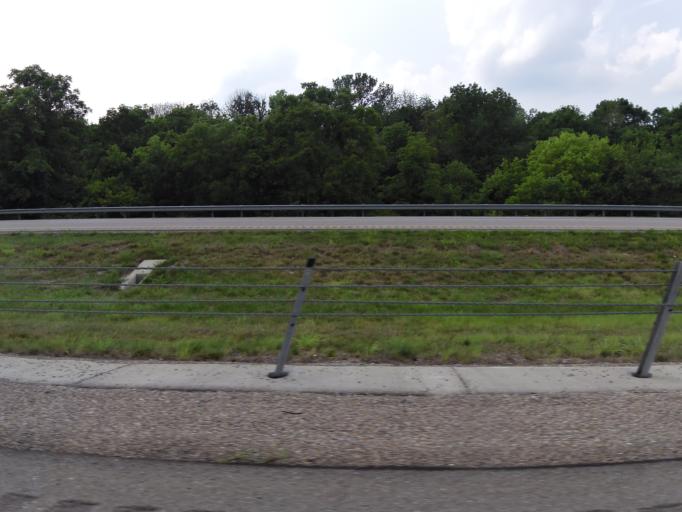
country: US
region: Kentucky
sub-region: Gallatin County
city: Warsaw
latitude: 38.7643
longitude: -84.7872
